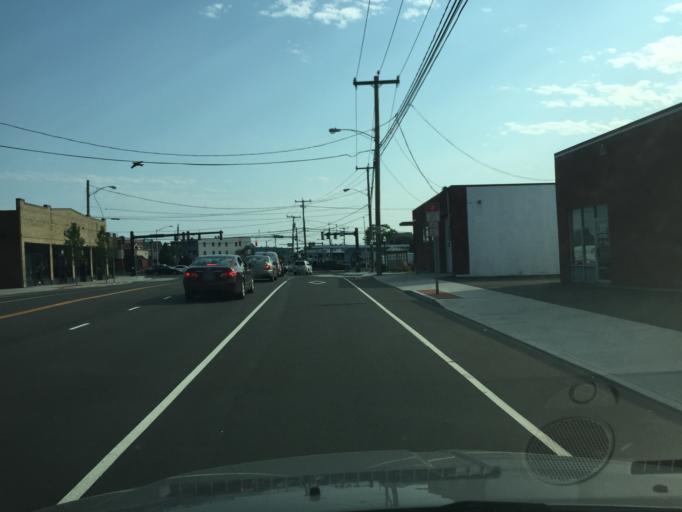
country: US
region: Connecticut
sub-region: Fairfield County
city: Stamford
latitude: 41.0514
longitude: -73.5271
